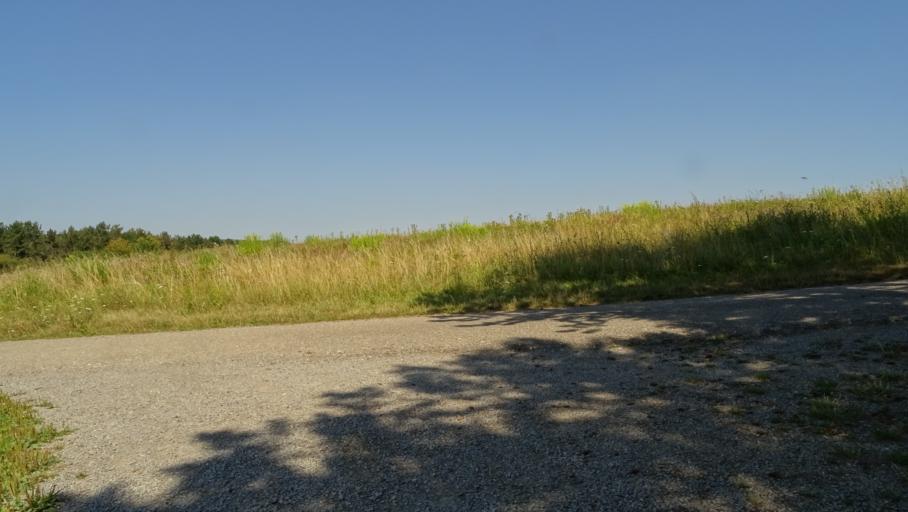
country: DE
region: Baden-Wuerttemberg
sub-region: Karlsruhe Region
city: Obrigheim
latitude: 49.3536
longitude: 9.1172
